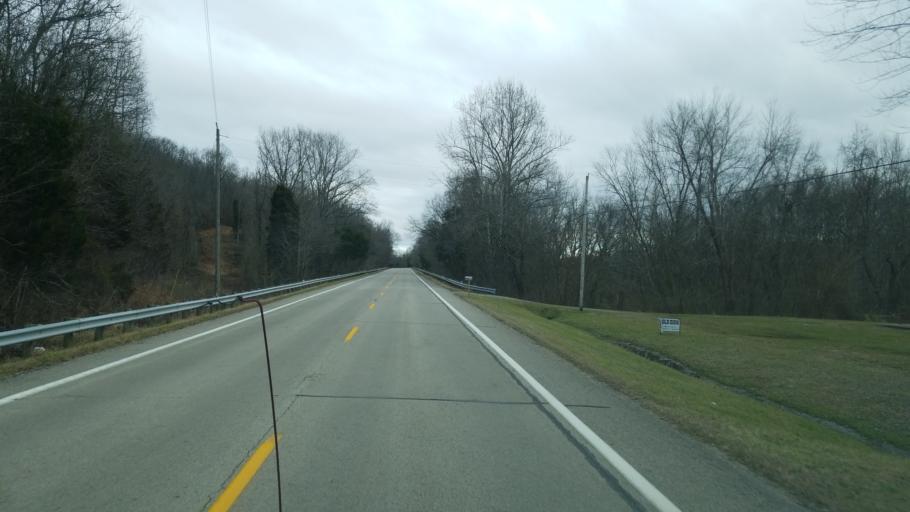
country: US
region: Kentucky
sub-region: Lewis County
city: Vanceburg
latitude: 38.6515
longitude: -83.3450
